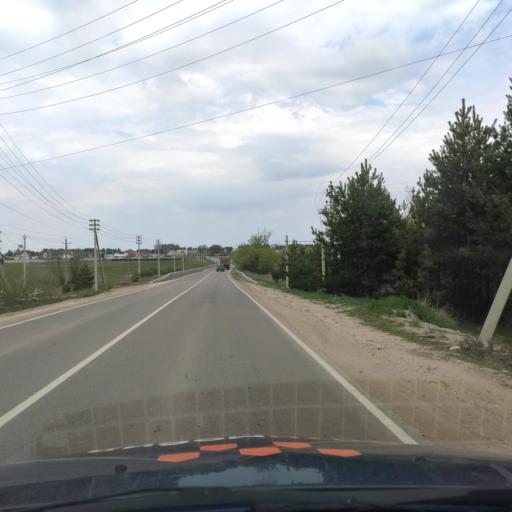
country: RU
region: Voronezj
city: Podgornoye
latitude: 51.8671
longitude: 39.1712
